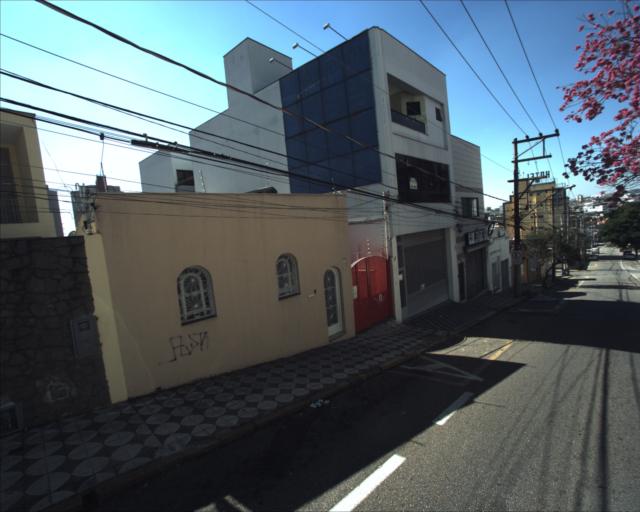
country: BR
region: Sao Paulo
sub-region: Sorocaba
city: Sorocaba
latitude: -23.5032
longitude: -47.4562
